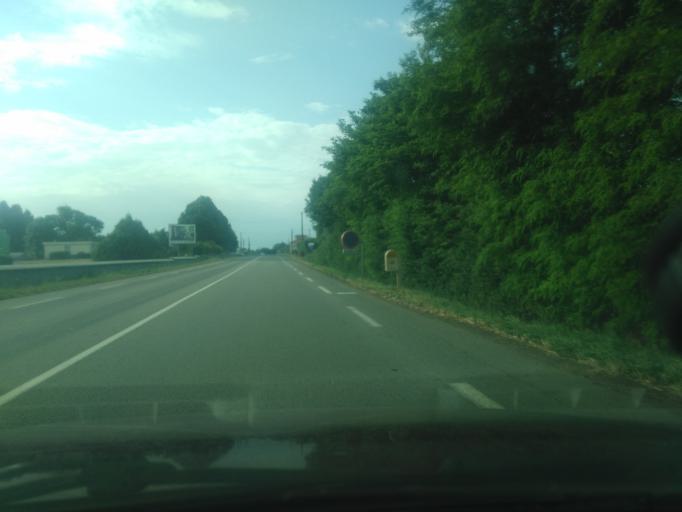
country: FR
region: Pays de la Loire
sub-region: Departement de la Vendee
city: Chantonnay
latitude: 46.7059
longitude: -1.0629
